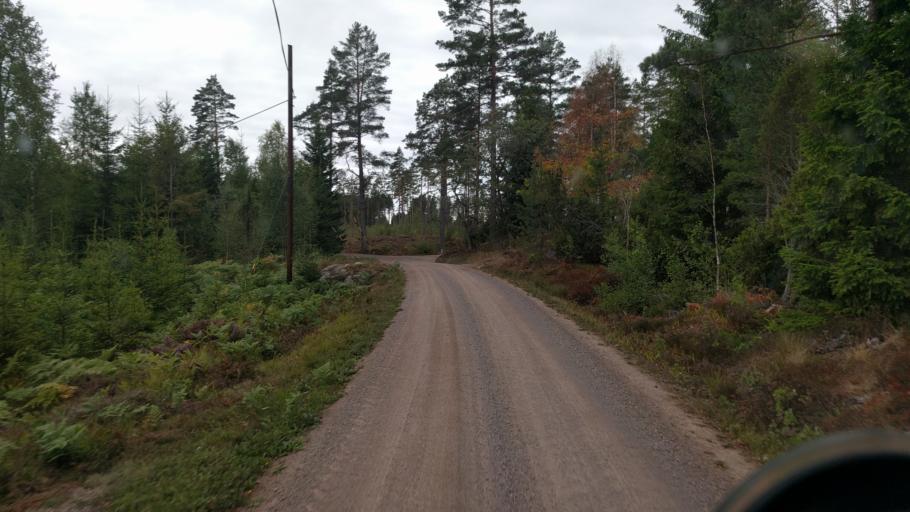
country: SE
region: Kalmar
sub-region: Vasterviks Kommun
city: Ankarsrum
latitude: 57.7641
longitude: 16.1822
